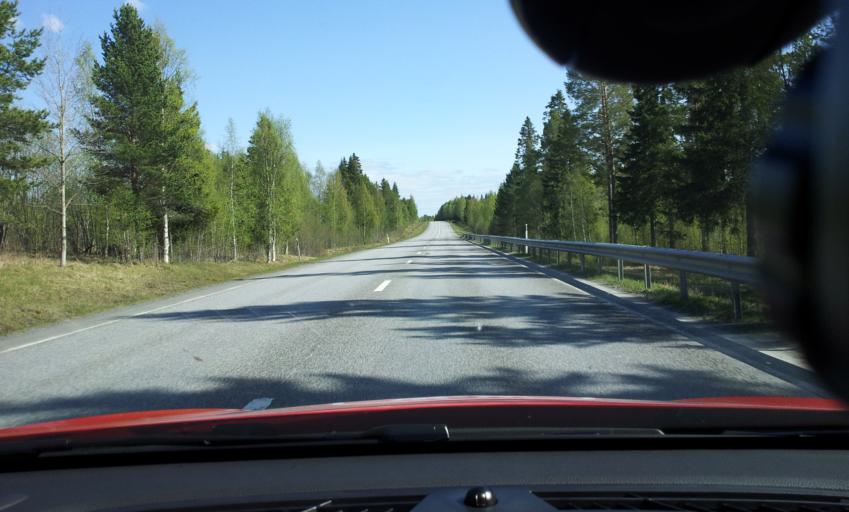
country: SE
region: Jaemtland
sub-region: Krokoms Kommun
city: Valla
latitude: 63.3299
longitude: 14.0359
